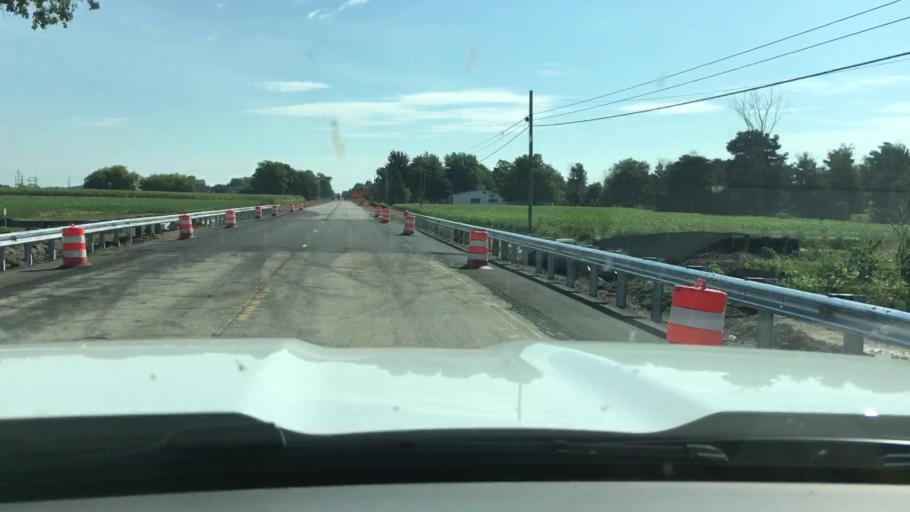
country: US
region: Michigan
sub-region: Saginaw County
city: Hemlock
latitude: 43.4124
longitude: -84.2764
